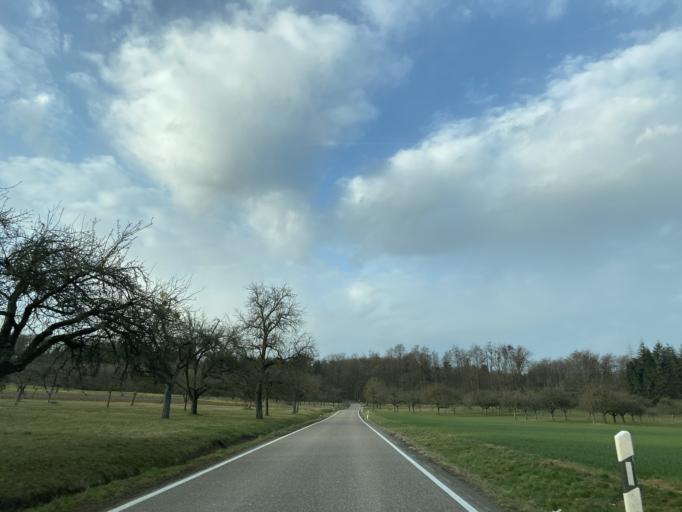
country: DE
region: Baden-Wuerttemberg
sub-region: Karlsruhe Region
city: Wiernsheim
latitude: 48.9046
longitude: 8.8869
